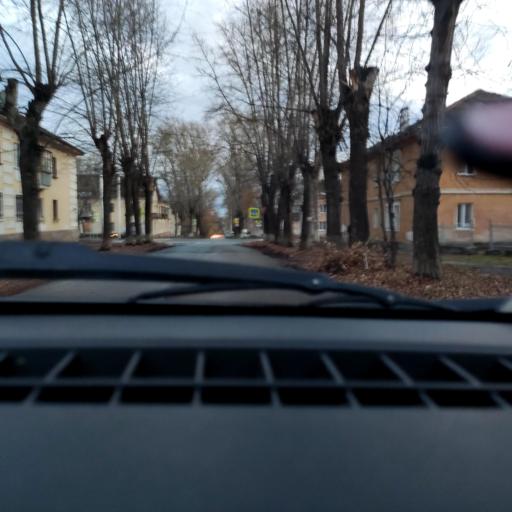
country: RU
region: Bashkortostan
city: Ufa
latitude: 54.8227
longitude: 56.0892
